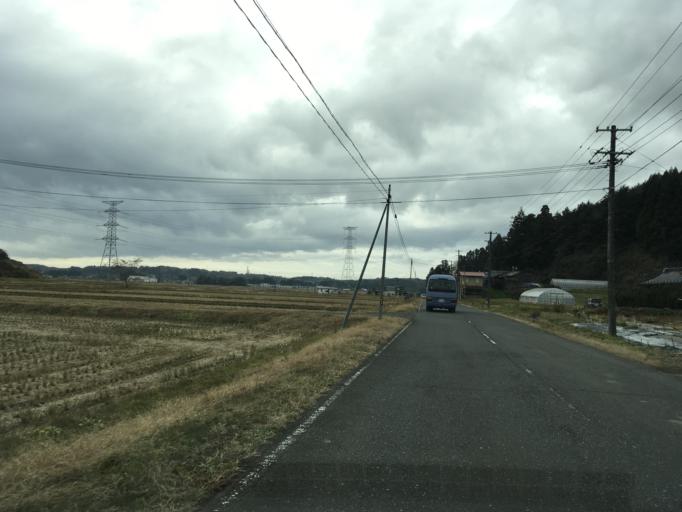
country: JP
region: Iwate
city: Ichinoseki
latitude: 38.8248
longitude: 141.0467
